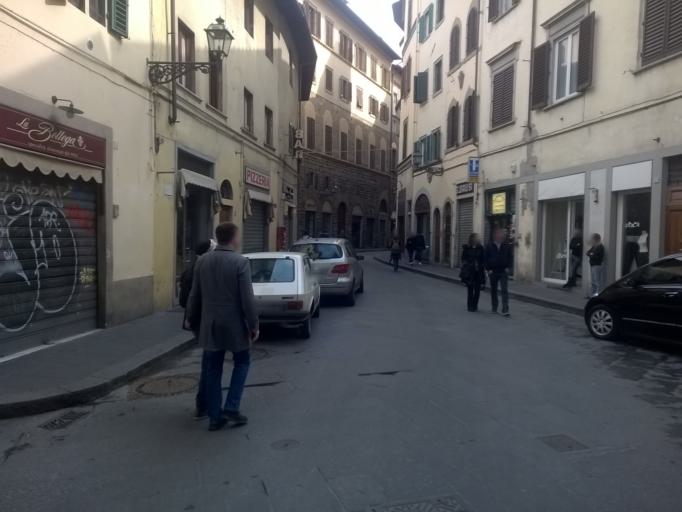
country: IT
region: Tuscany
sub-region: Province of Florence
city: Florence
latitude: 43.7681
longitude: 11.2581
